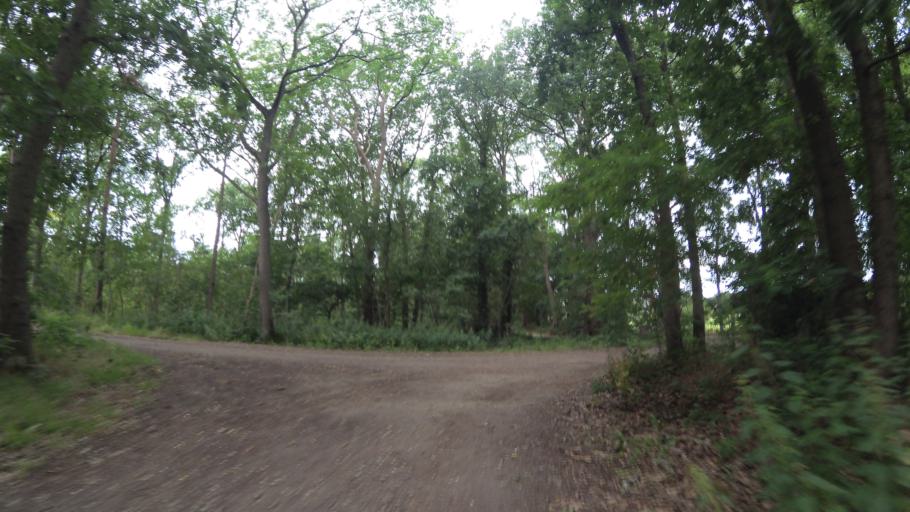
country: NL
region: North Brabant
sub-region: Gemeente Breda
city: Hoge Vucht
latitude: 51.6373
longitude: 4.7985
